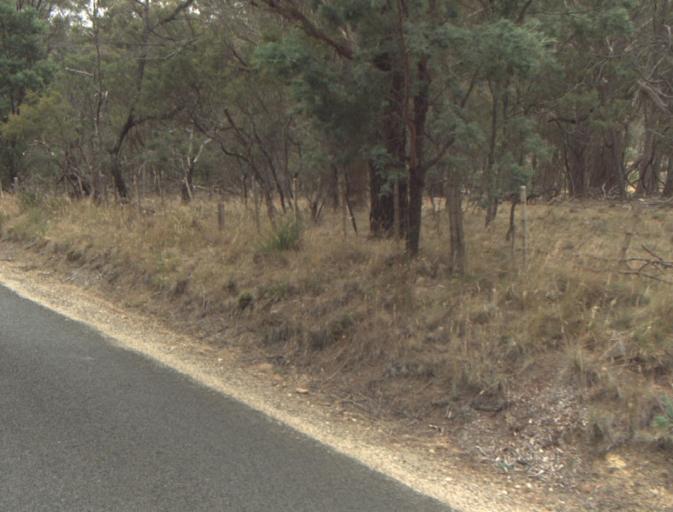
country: AU
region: Tasmania
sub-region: Northern Midlands
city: Evandale
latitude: -41.5117
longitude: 147.3324
